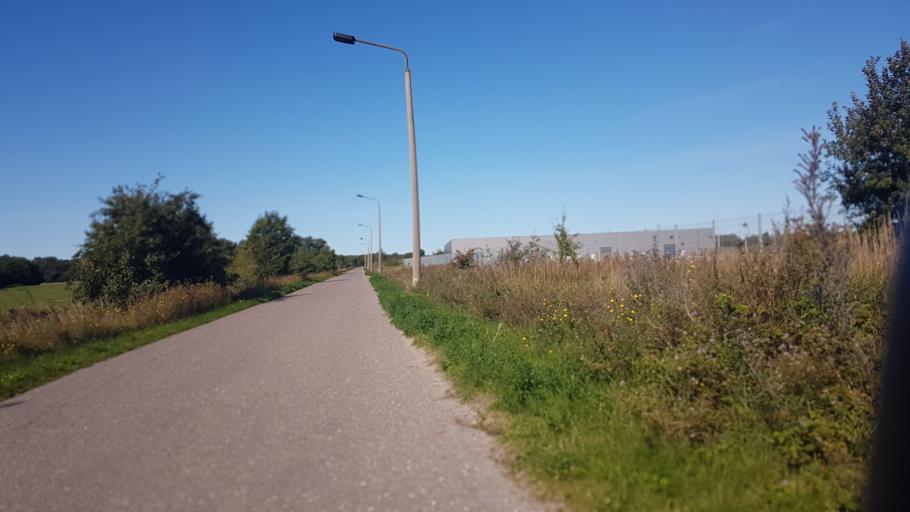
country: DE
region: Mecklenburg-Vorpommern
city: Sagard
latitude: 54.4930
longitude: 13.5632
